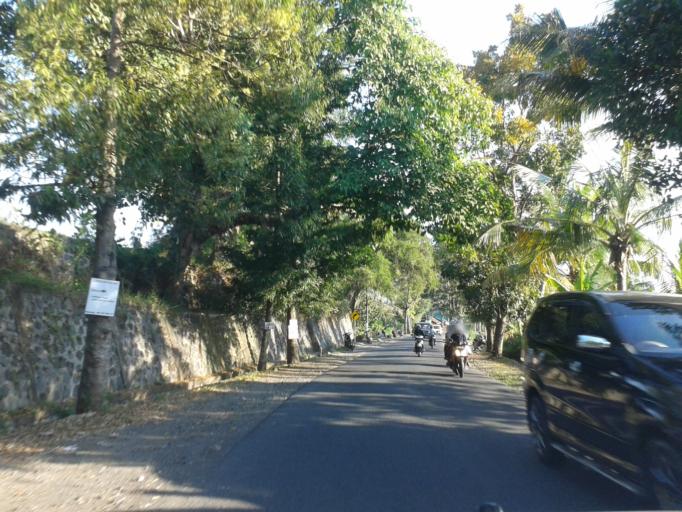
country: ID
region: Bali
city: Banjar Wangsian
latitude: -8.5015
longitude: 115.4040
